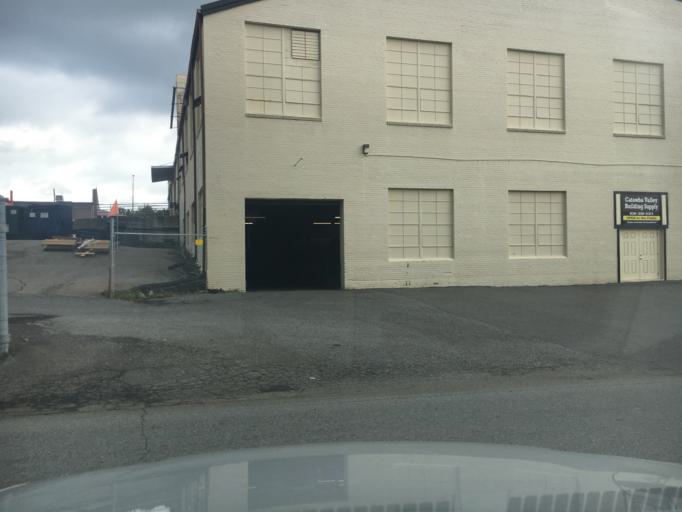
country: US
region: North Carolina
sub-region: Catawba County
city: Hickory
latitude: 35.7299
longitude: -81.3439
